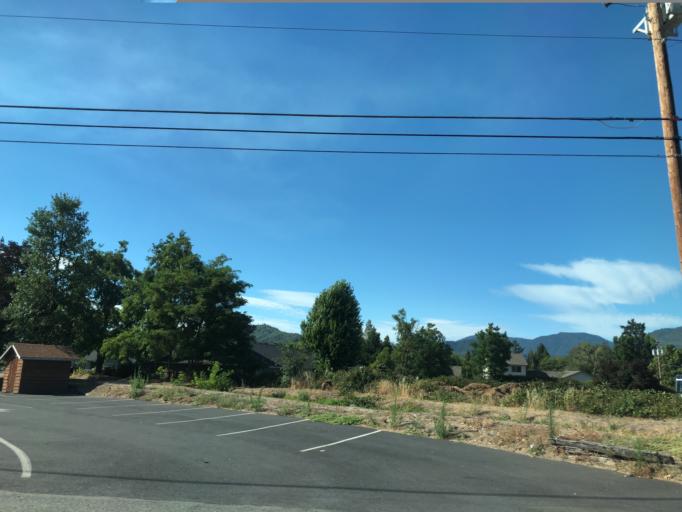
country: US
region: Oregon
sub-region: Josephine County
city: Grants Pass
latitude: 42.4242
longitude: -123.3373
